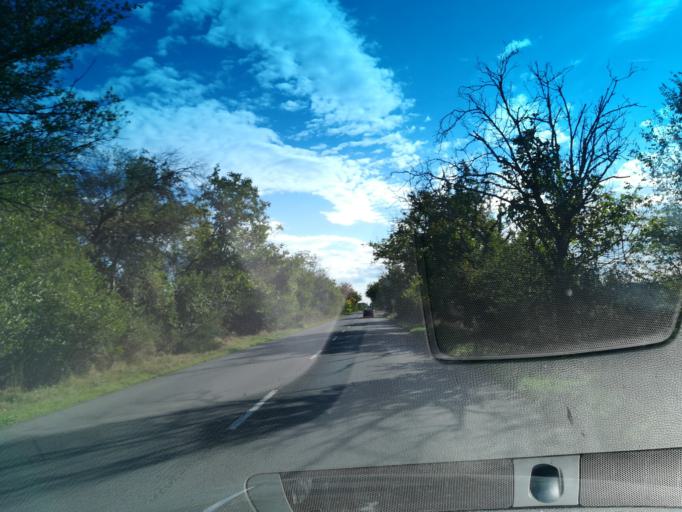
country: BG
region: Stara Zagora
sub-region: Obshtina Stara Zagora
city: Stara Zagora
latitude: 42.3703
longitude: 25.6532
